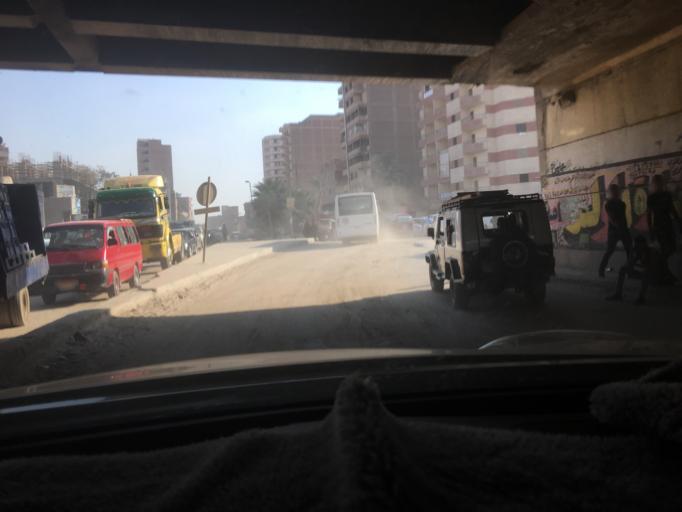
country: EG
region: Muhafazat al Qalyubiyah
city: Al Khankah
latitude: 30.1659
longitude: 31.3831
